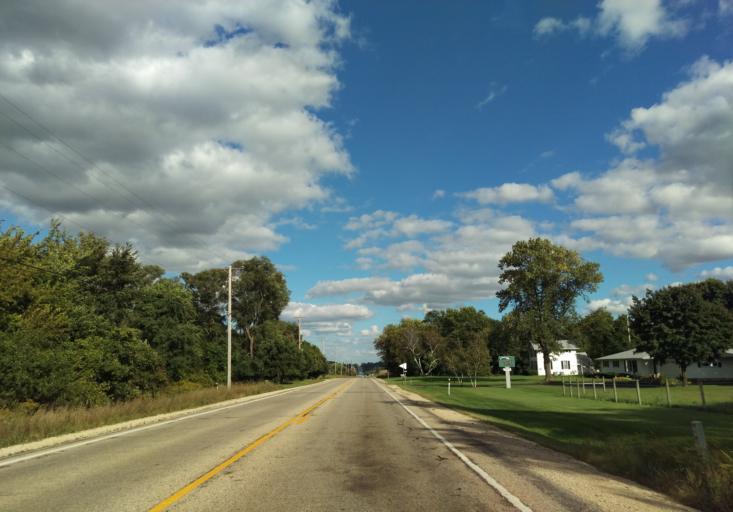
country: US
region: Wisconsin
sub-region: Rock County
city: Janesville
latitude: 42.7302
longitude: -89.0792
